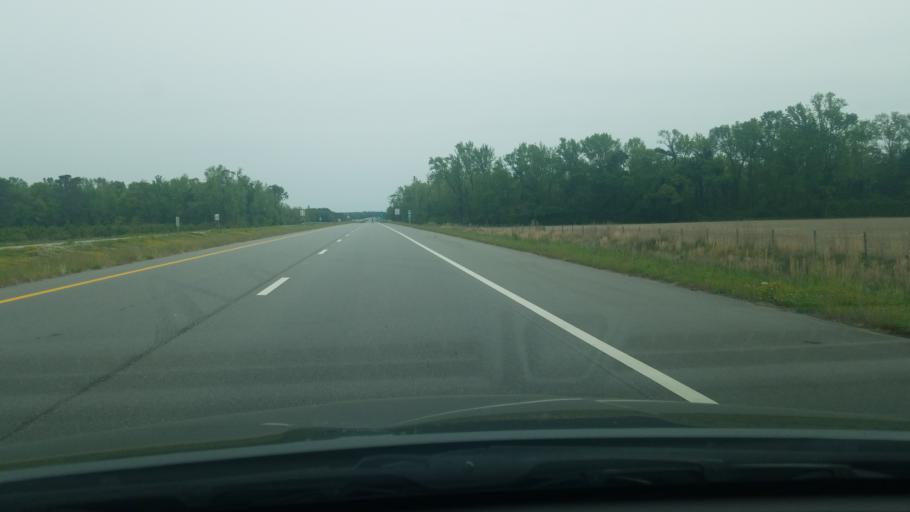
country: US
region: North Carolina
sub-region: Jones County
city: Maysville
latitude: 34.9799
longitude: -77.2385
